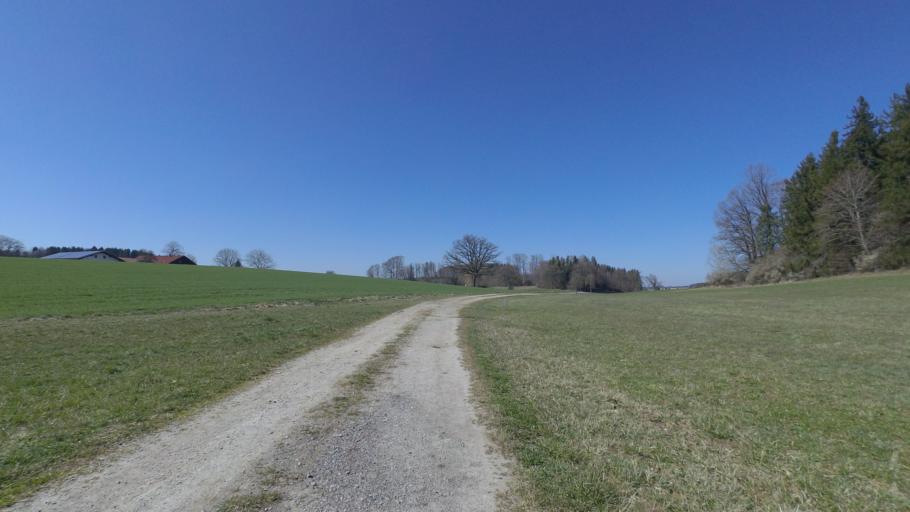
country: DE
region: Bavaria
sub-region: Upper Bavaria
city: Seeon-Seebruck
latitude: 47.9379
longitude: 12.5034
